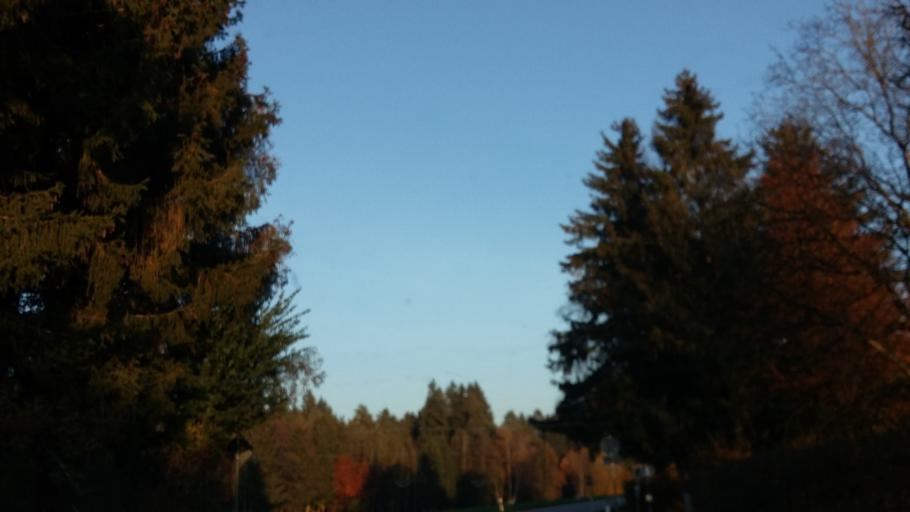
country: DE
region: Bavaria
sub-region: Upper Bavaria
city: Eggstatt
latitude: 47.8919
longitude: 12.3773
